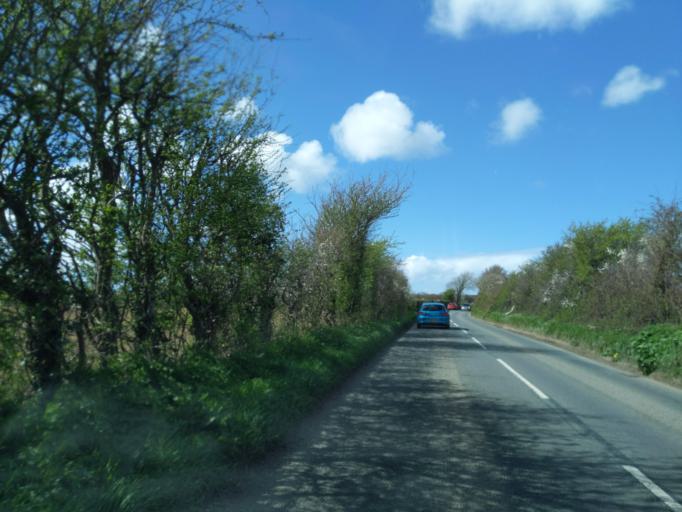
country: GB
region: England
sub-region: Cornwall
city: Wadebridge
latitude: 50.5374
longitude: -4.8523
